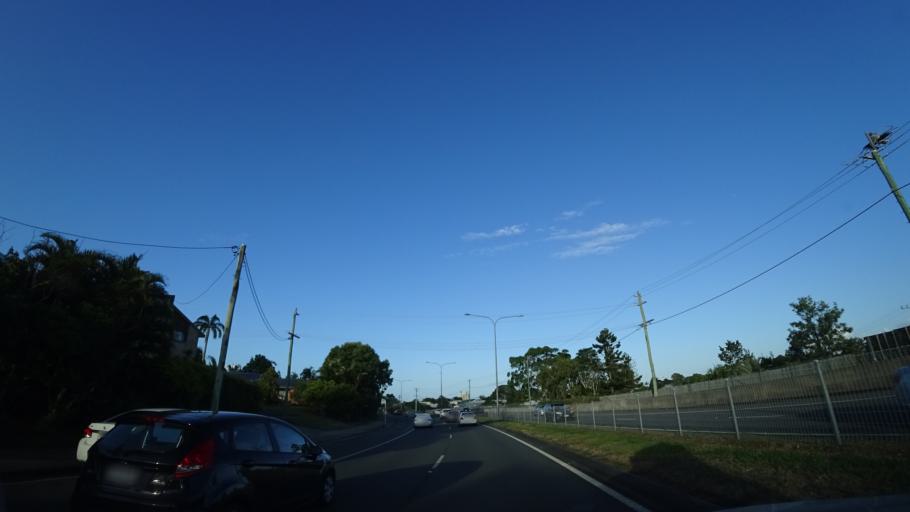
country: AU
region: Queensland
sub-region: Sunshine Coast
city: Buderim
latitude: -26.6546
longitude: 153.0771
